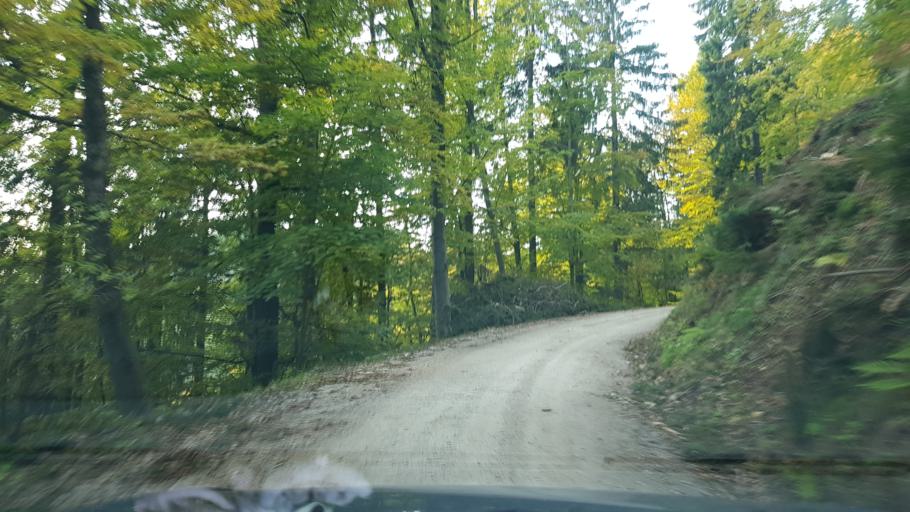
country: SI
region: Slovenj Gradec
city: Legen
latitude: 46.5257
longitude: 15.1272
